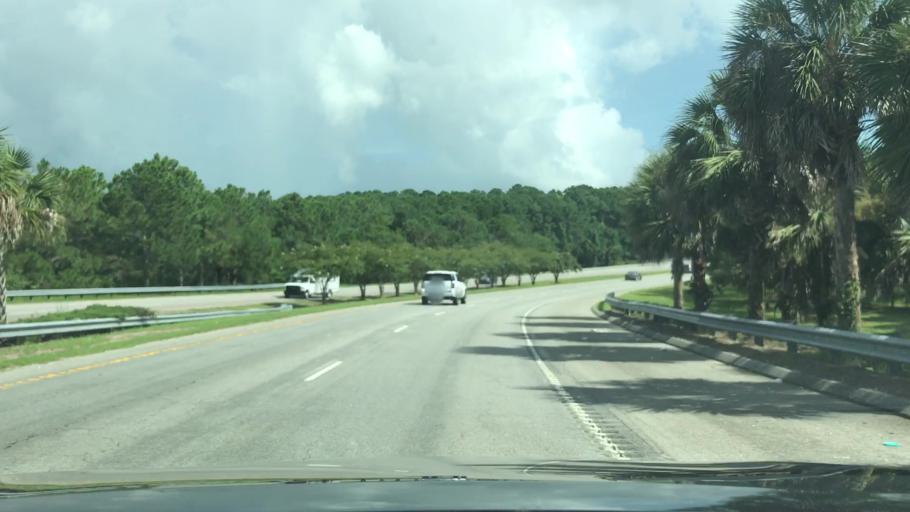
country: US
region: South Carolina
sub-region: Beaufort County
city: Hilton Head Island
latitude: 32.2138
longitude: -80.7383
